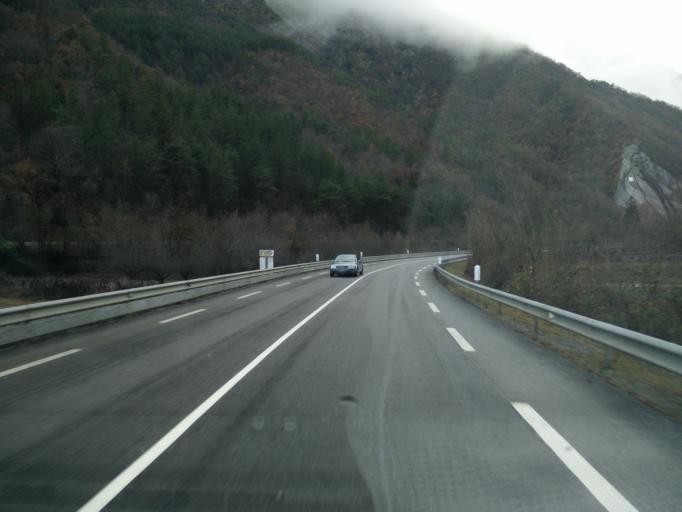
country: FR
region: Provence-Alpes-Cote d'Azur
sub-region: Departement des Alpes-Maritimes
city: Gilette
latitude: 43.9283
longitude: 7.1020
